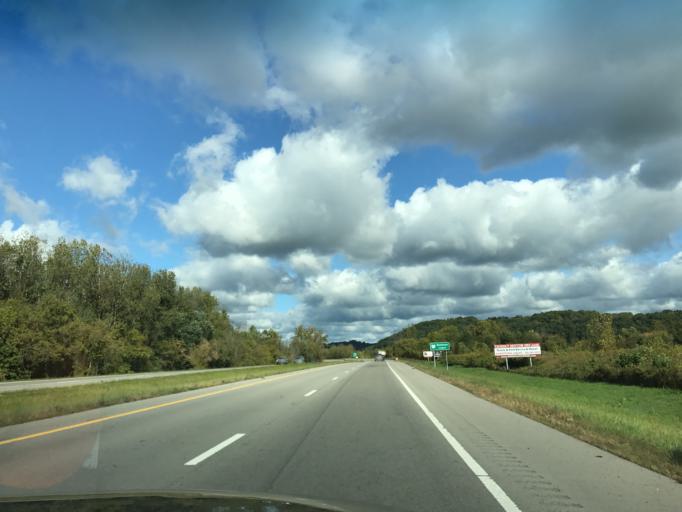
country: US
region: Ohio
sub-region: Hocking County
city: Logan
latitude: 39.5056
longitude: -82.3563
